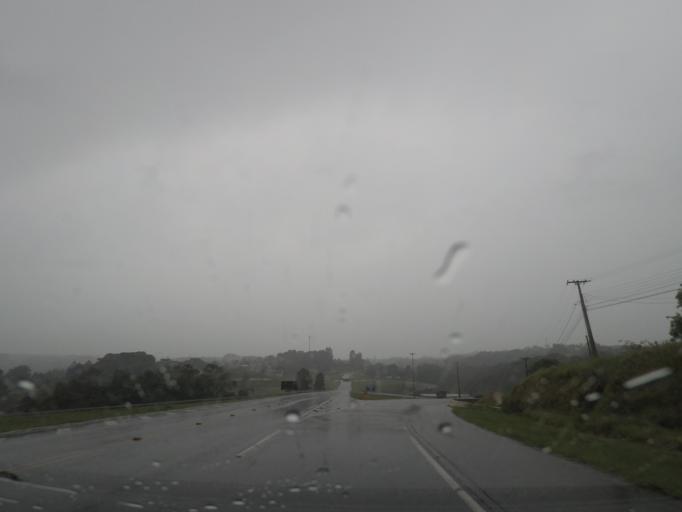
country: BR
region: Parana
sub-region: Almirante Tamandare
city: Almirante Tamandare
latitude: -25.3526
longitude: -49.2836
